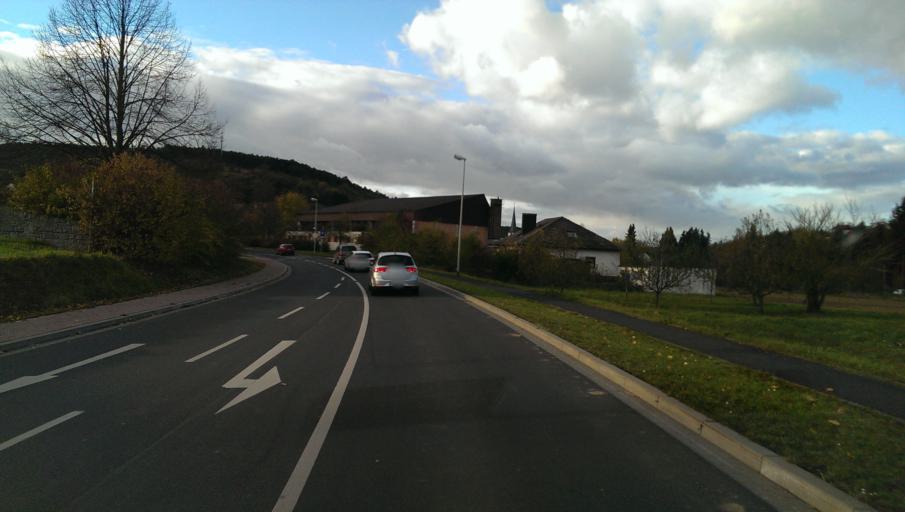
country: DE
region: Bavaria
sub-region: Regierungsbezirk Unterfranken
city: Zellingen
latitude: 49.8634
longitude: 9.8039
